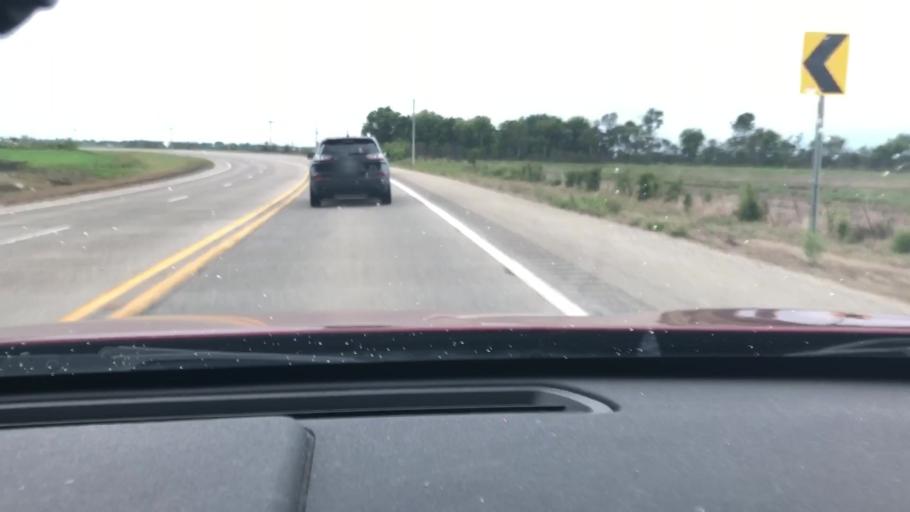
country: US
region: Arkansas
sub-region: Lafayette County
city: Lewisville
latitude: 33.3990
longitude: -93.7446
